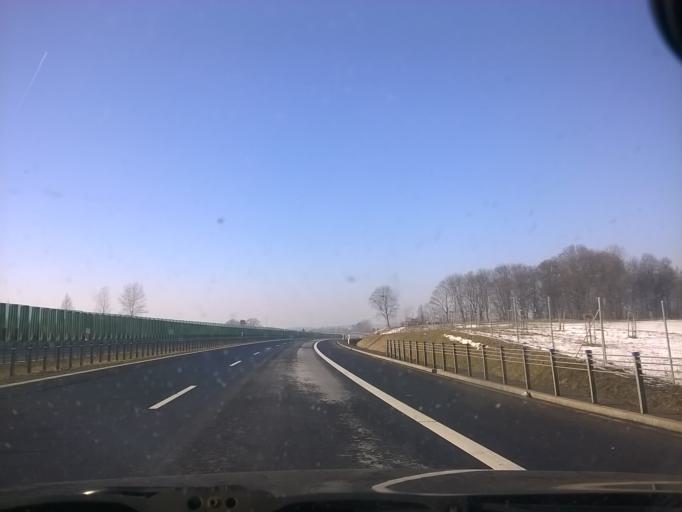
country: PL
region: Warmian-Masurian Voivodeship
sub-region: Powiat olsztynski
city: Biskupiec
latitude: 53.8467
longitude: 20.9820
